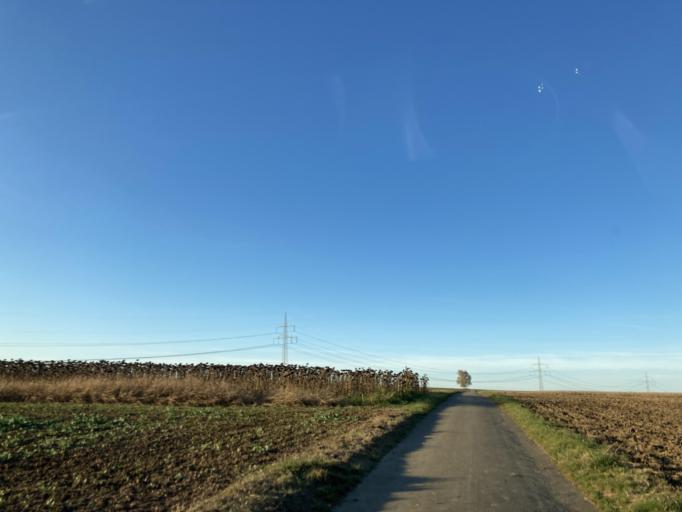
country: DE
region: Baden-Wuerttemberg
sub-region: Tuebingen Region
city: Hirrlingen
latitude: 48.4138
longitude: 8.8829
